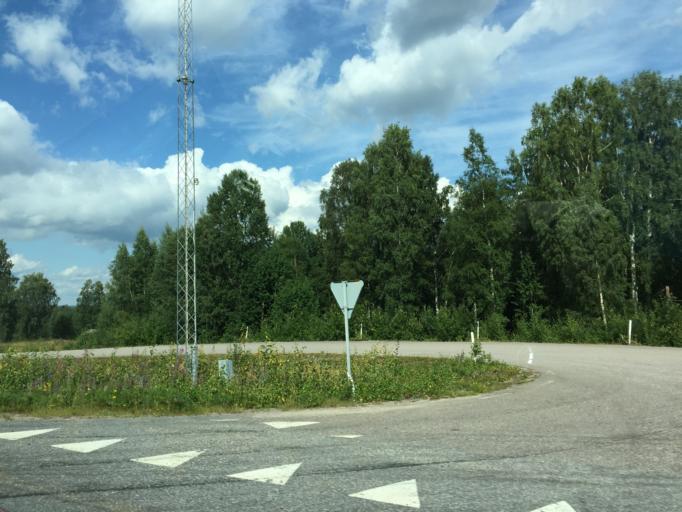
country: SE
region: Gaevleborg
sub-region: Bollnas Kommun
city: Kilafors
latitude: 61.2008
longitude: 16.7588
